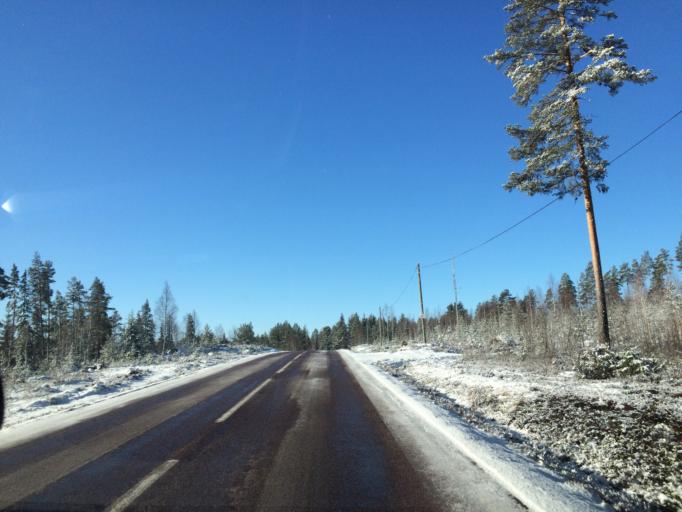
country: SE
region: Dalarna
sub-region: Vansbro Kommun
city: Vansbro
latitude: 60.7396
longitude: 14.1287
